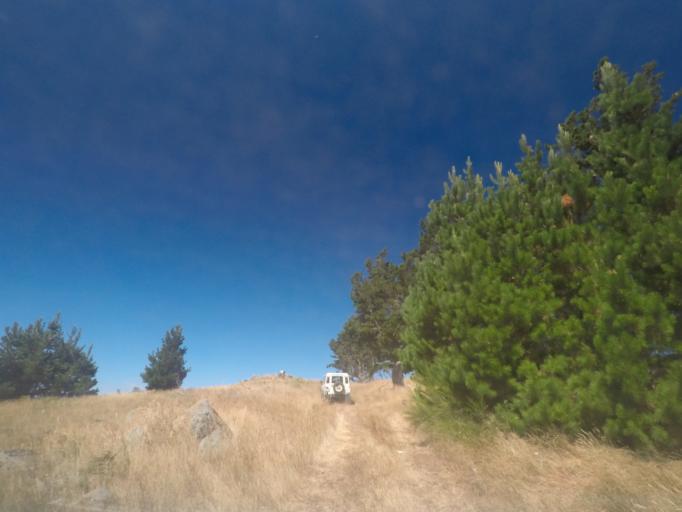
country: PT
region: Madeira
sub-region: Funchal
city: Nossa Senhora do Monte
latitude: 32.7095
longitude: -16.9097
